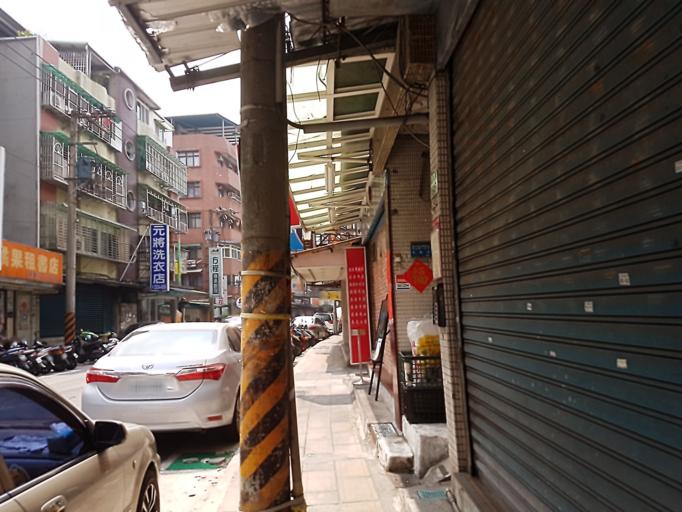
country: TW
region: Taipei
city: Taipei
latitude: 24.9954
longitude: 121.5463
